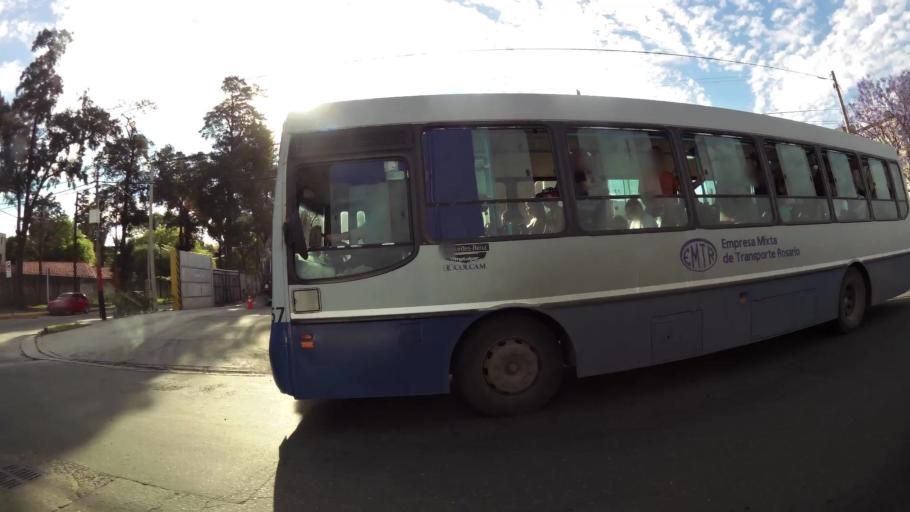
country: AR
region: Santa Fe
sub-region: Departamento de Rosario
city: Rosario
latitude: -32.9828
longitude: -60.6714
